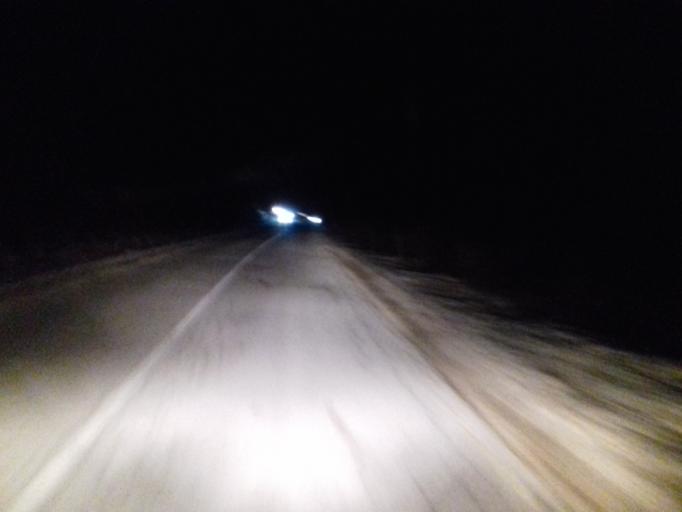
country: BA
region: Federation of Bosnia and Herzegovina
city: Gracanica
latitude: 43.7310
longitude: 18.3055
